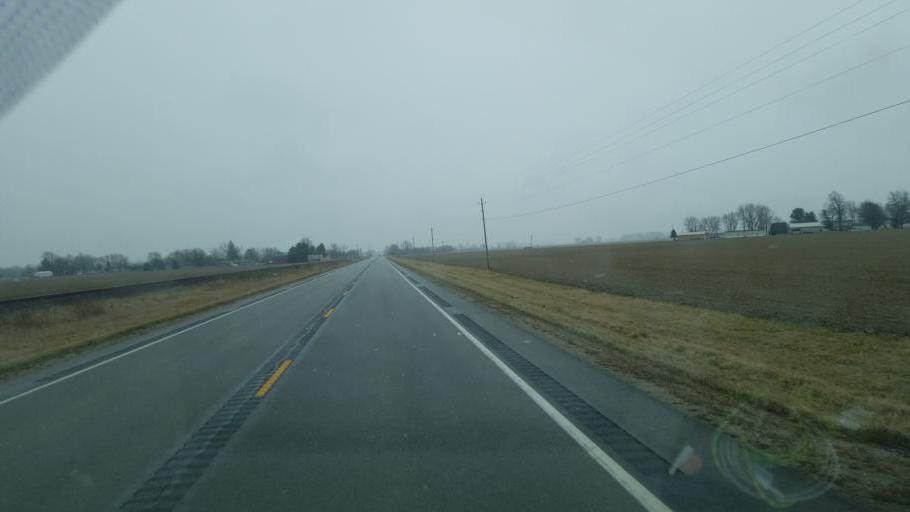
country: US
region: Indiana
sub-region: Wabash County
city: Wabash
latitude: 40.7434
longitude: -85.7980
